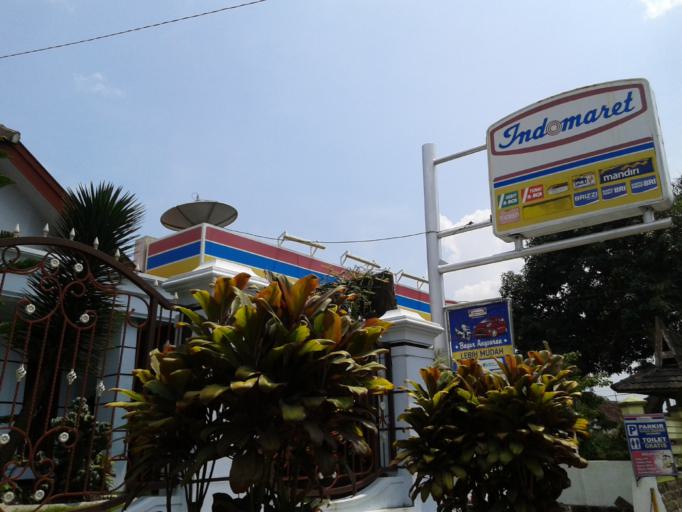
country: ID
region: East Java
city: Lawang
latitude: -7.8215
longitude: 112.7081
